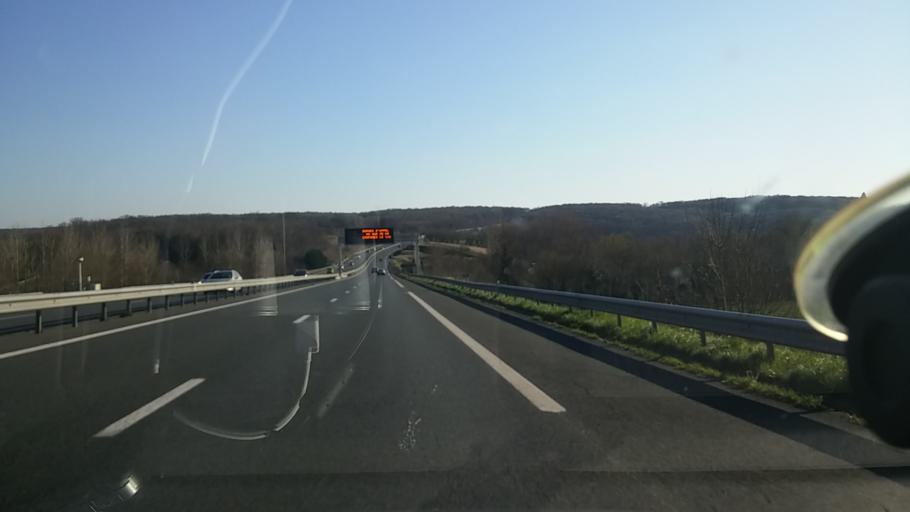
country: FR
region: Centre
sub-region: Departement de l'Indre
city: Saint-Marcel
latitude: 46.6328
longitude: 1.5496
